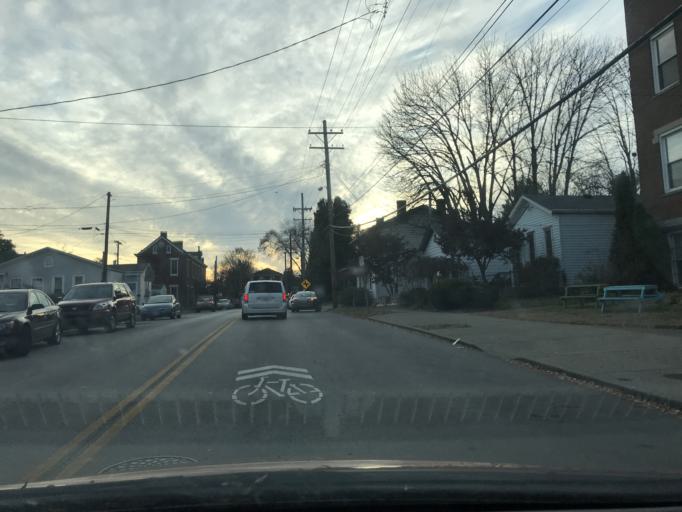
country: US
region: Indiana
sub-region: Clark County
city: Jeffersonville
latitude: 38.2468
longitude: -85.7279
